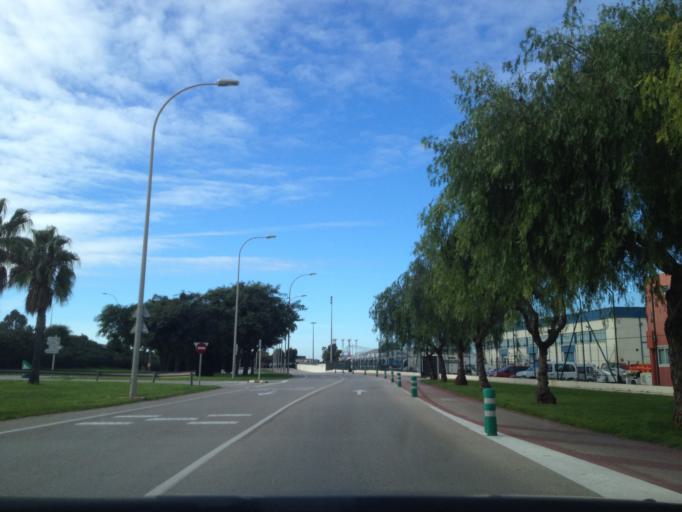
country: ES
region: Balearic Islands
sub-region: Illes Balears
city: s'Arenal
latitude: 39.5490
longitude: 2.7278
